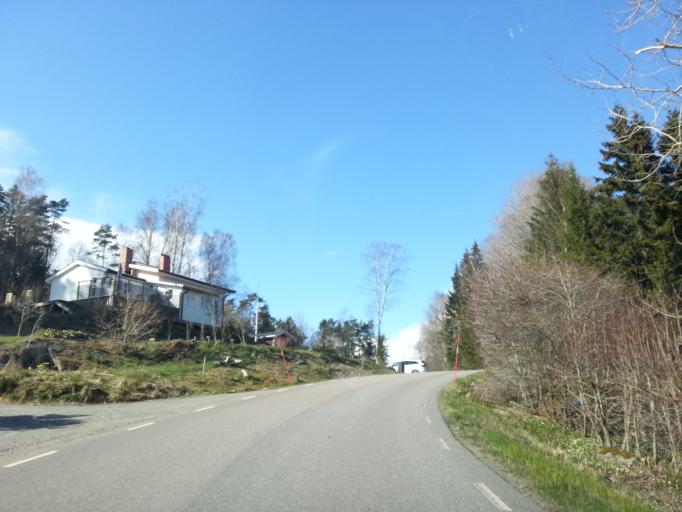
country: SE
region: Vaestra Goetaland
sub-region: Kungalvs Kommun
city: Diserod
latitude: 57.9546
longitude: 12.0172
